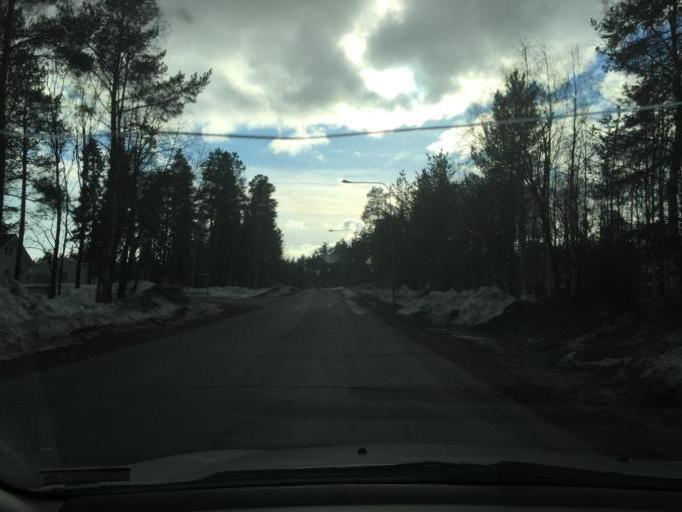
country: SE
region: Norrbotten
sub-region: Lulea Kommun
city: Lulea
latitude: 65.5938
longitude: 22.2316
